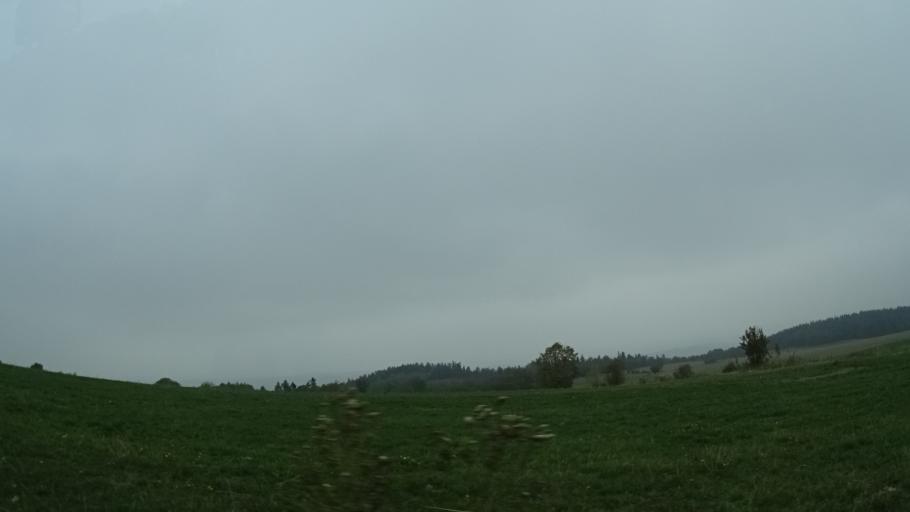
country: DE
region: Thuringia
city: Oberhain
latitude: 50.6403
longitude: 11.1258
